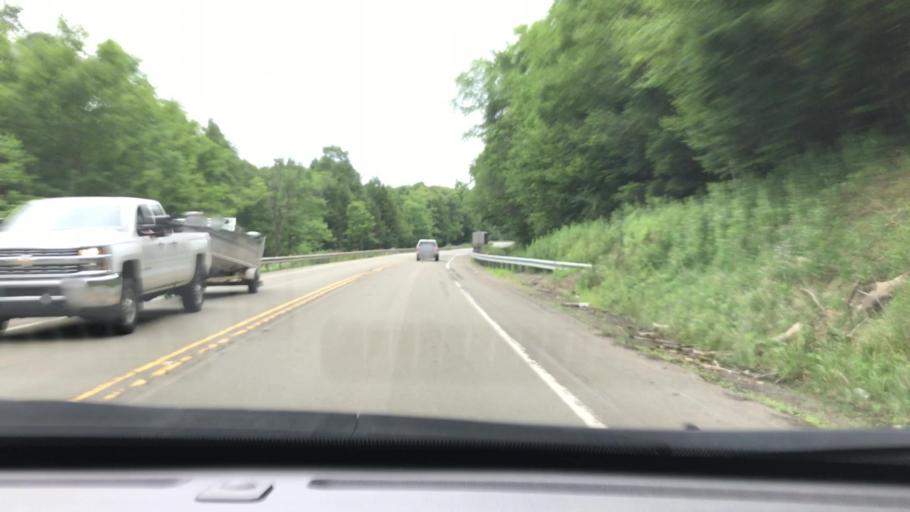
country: US
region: Pennsylvania
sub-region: McKean County
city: Kane
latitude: 41.6653
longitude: -78.6815
